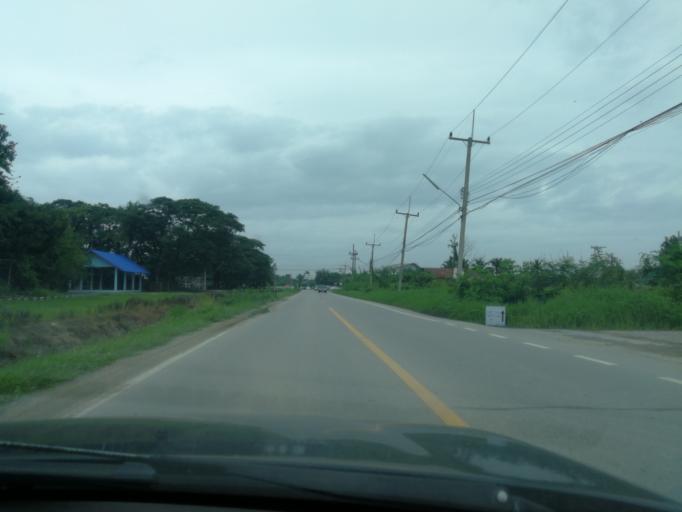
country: TH
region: Chiang Mai
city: San Pa Tong
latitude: 18.6244
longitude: 98.8982
